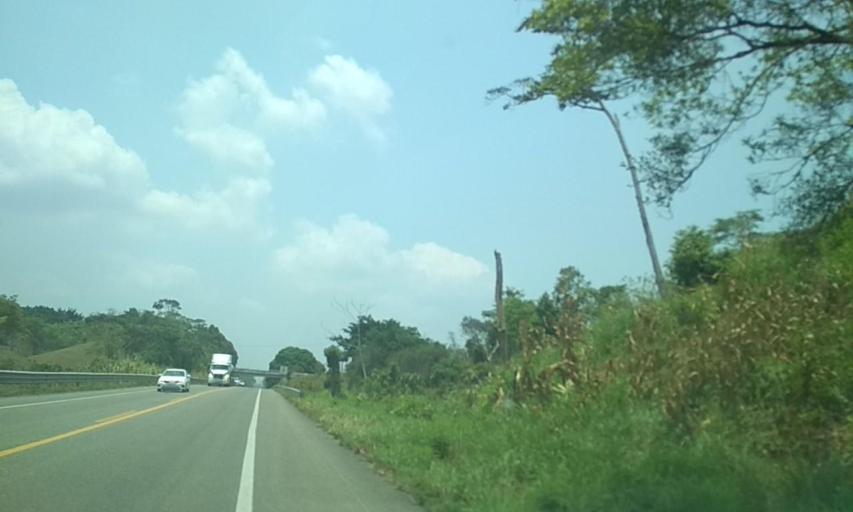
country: MX
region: Tabasco
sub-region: Huimanguillo
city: Francisco Rueda
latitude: 17.6721
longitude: -93.8723
